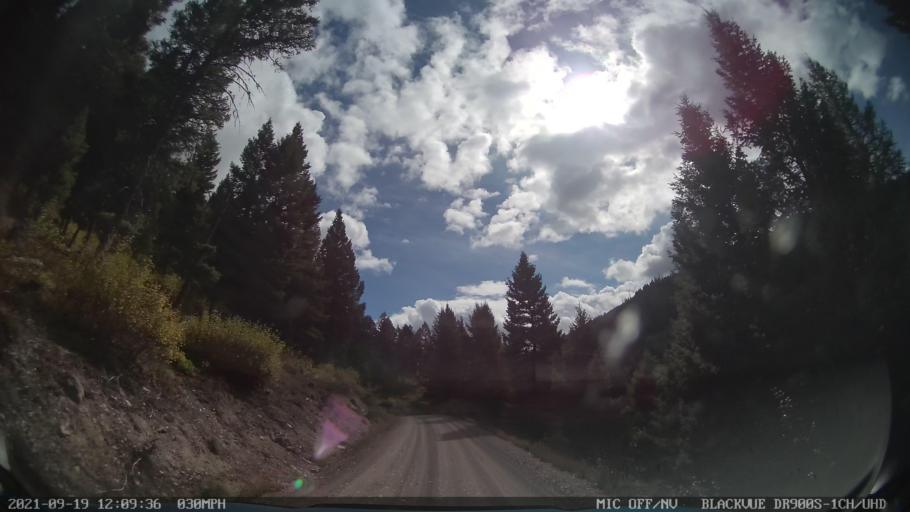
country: US
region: Montana
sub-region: Missoula County
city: Seeley Lake
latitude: 47.1827
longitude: -113.3899
